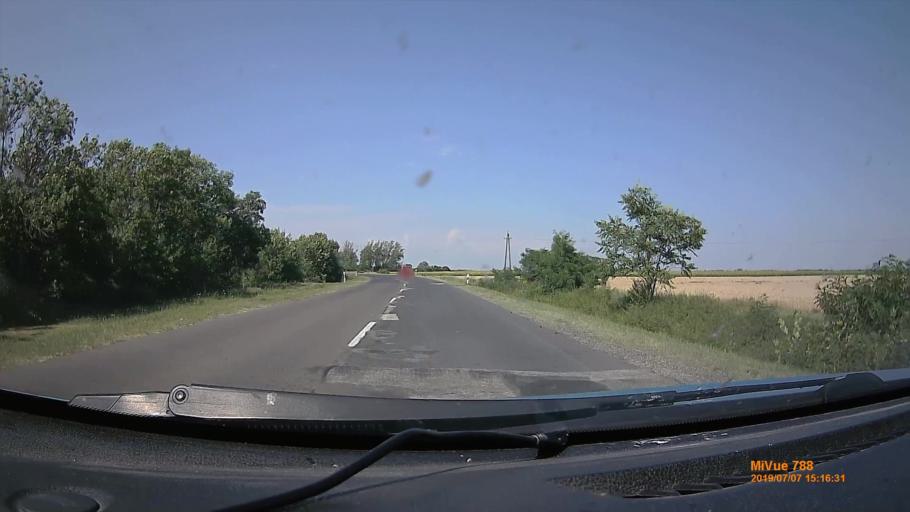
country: HU
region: Jasz-Nagykun-Szolnok
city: Ujszasz
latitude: 47.3285
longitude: 20.0928
